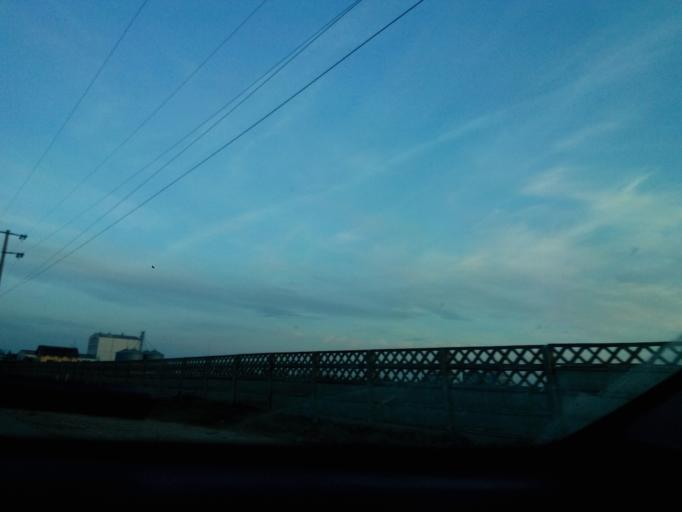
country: RO
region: Prahova
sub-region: Comuna Paulesti
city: Gageni
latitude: 44.9890
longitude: 25.9151
